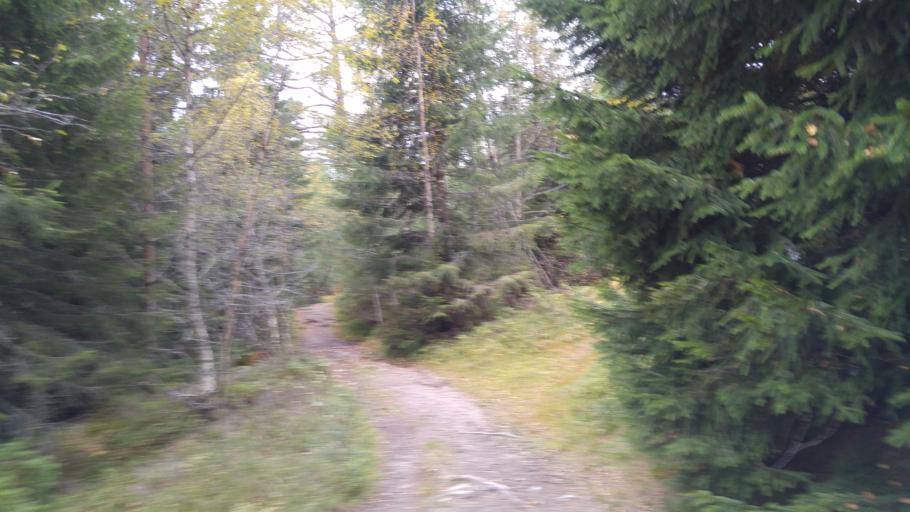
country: NO
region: Sor-Trondelag
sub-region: Trondheim
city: Trondheim
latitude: 63.4232
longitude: 10.3204
